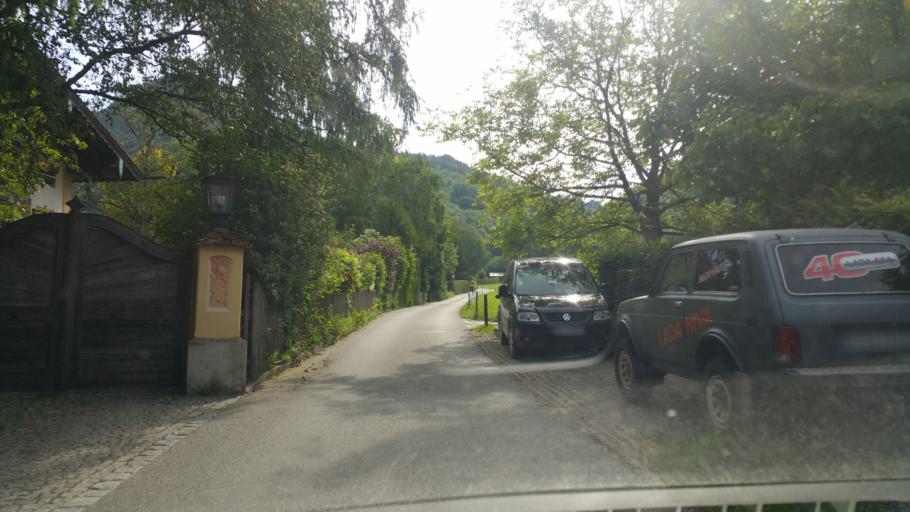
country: DE
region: Bavaria
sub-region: Upper Bavaria
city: Aschau im Chiemgau
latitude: 47.7753
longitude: 12.3303
